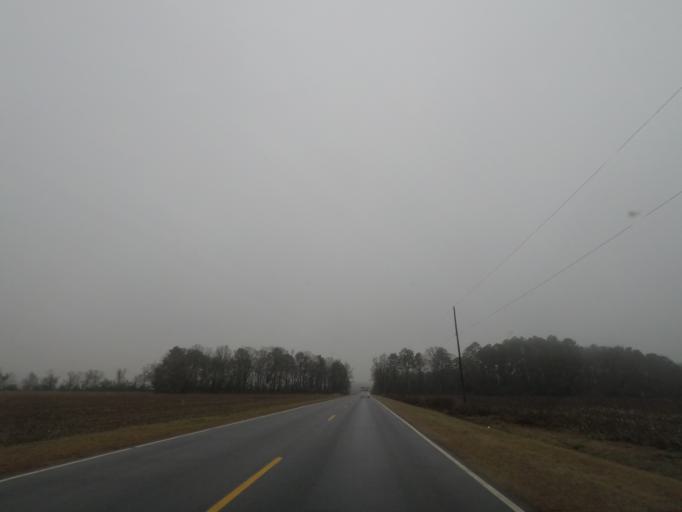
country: US
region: North Carolina
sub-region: Scotland County
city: Laurinburg
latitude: 34.7861
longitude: -79.4299
